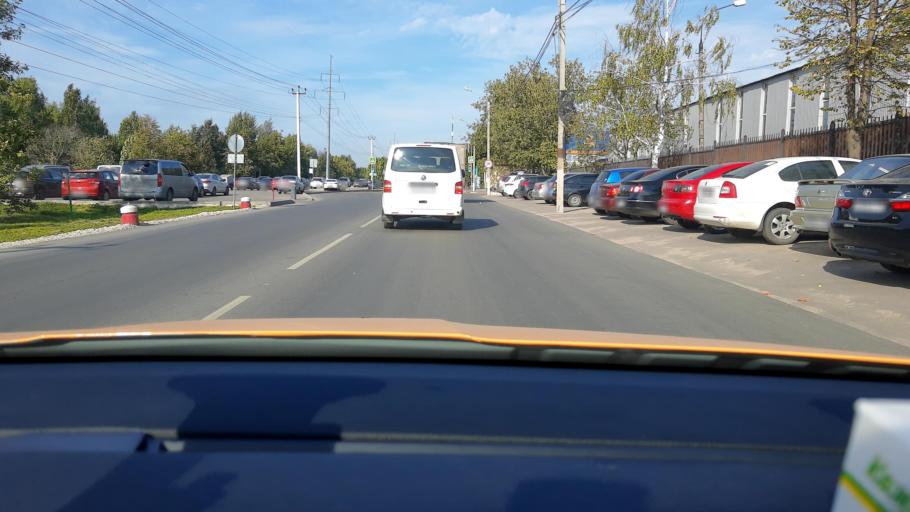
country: RU
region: Moskovskaya
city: Mosrentgen
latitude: 55.6116
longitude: 37.4594
